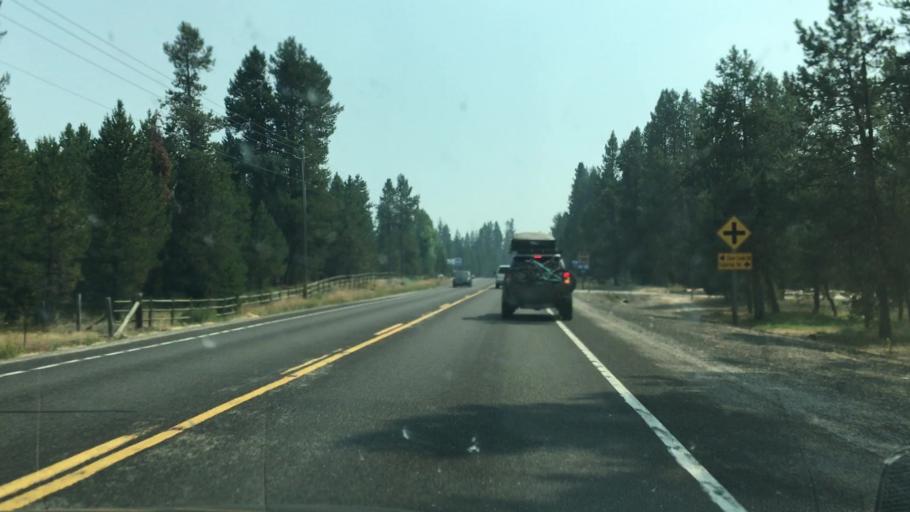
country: US
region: Idaho
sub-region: Valley County
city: Cascade
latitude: 44.4096
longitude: -115.9998
